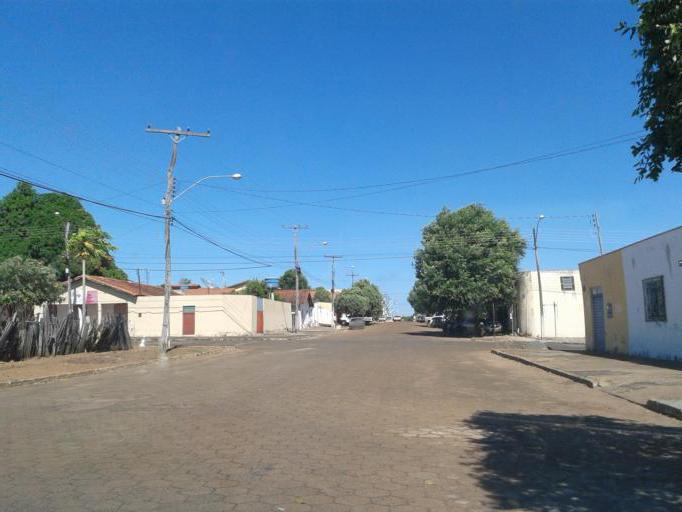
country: BR
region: Goias
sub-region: Sao Miguel Do Araguaia
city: Sao Miguel do Araguaia
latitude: -13.2714
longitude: -50.1599
